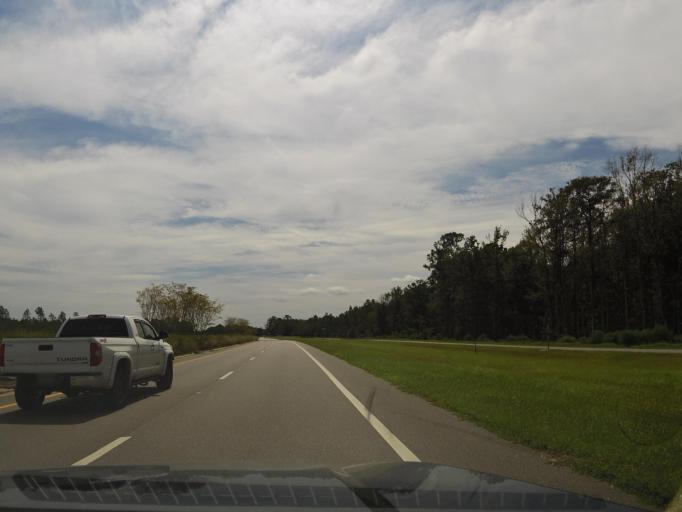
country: US
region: Florida
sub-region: Saint Johns County
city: Fruit Cove
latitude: 30.0313
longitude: -81.5263
